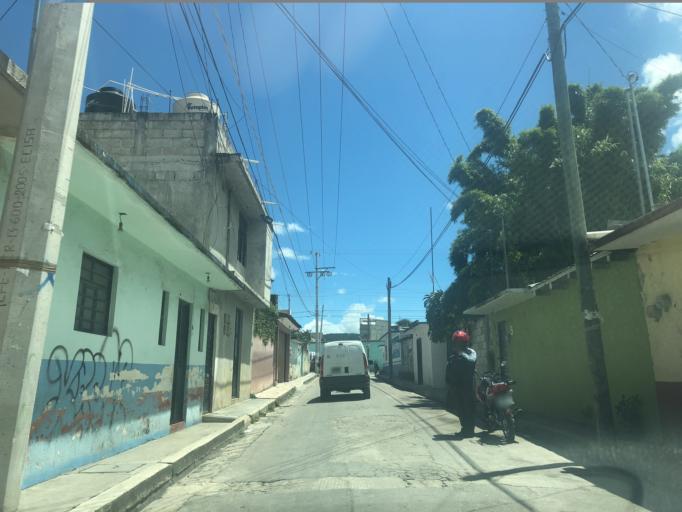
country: MX
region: Chiapas
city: San Cristobal de las Casas
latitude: 16.7173
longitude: -92.6412
